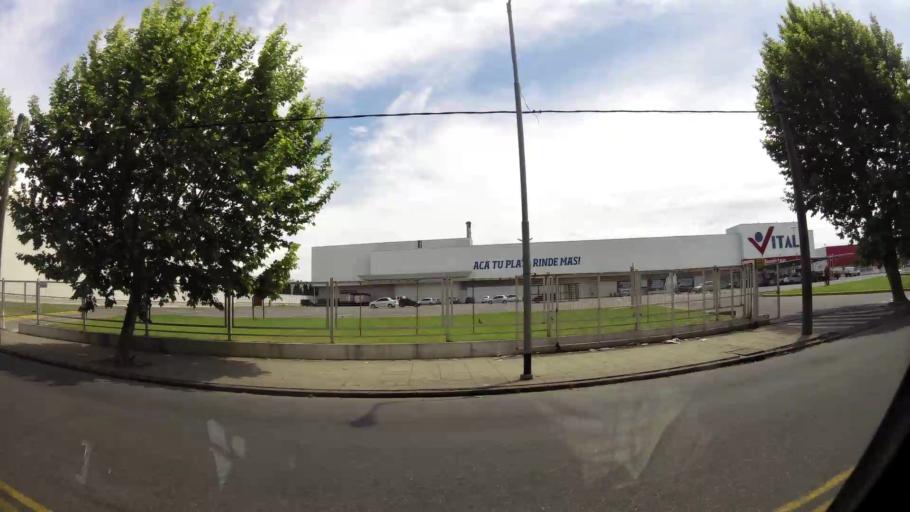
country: AR
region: Buenos Aires
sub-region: Partido de Avellaneda
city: Avellaneda
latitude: -34.6646
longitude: -58.3890
